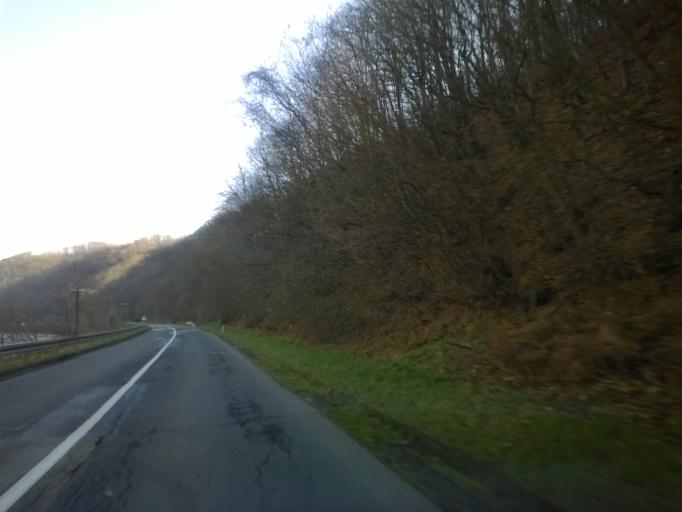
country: RS
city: Radenka
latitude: 44.6565
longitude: 21.7784
